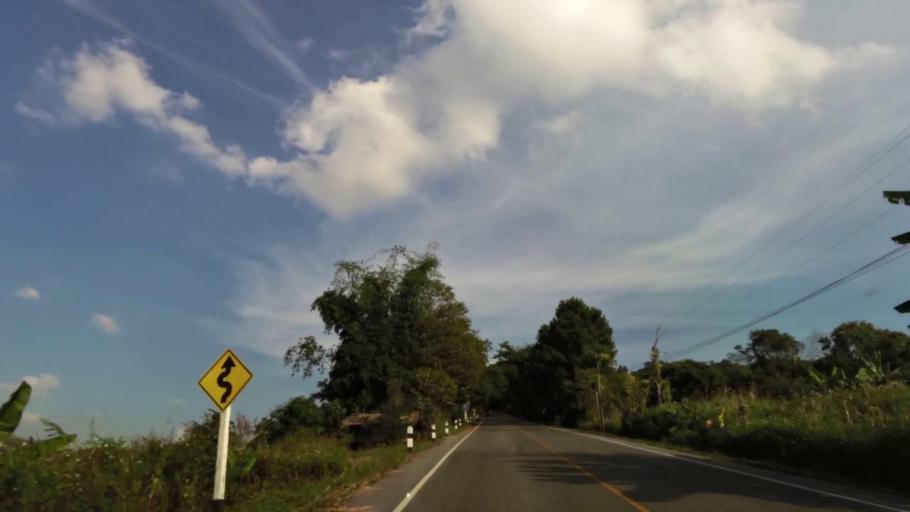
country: TH
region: Chiang Rai
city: Khun Tan
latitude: 19.8711
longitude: 100.3240
